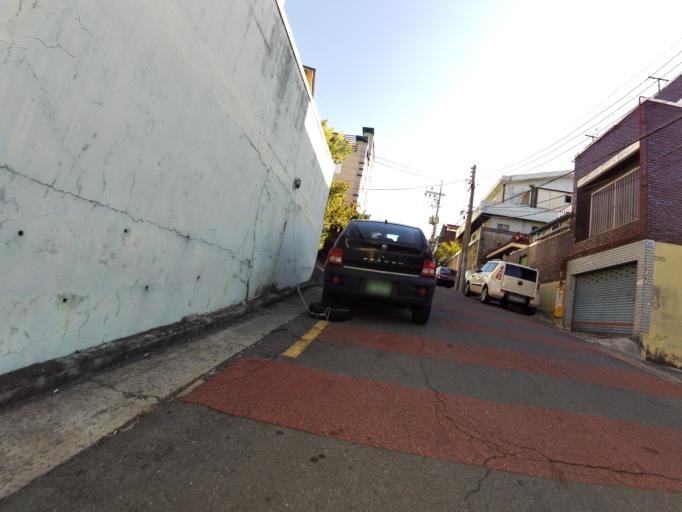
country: KR
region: Daegu
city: Daegu
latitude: 35.8621
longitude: 128.6418
